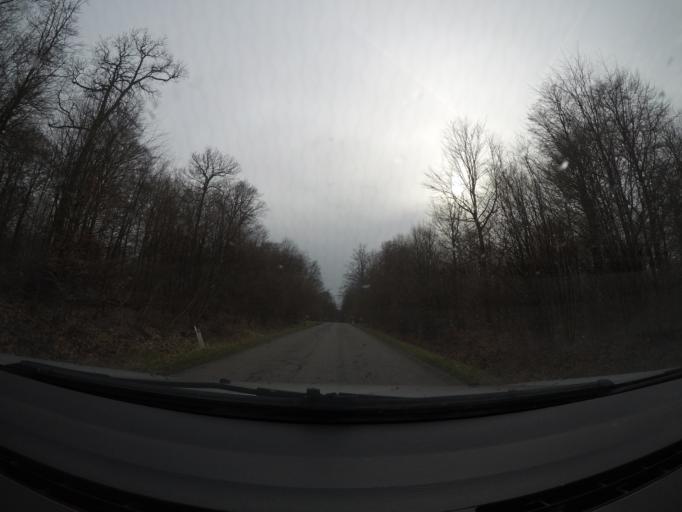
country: BE
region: Wallonia
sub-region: Province du Luxembourg
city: Martelange
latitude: 49.7830
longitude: 5.6856
